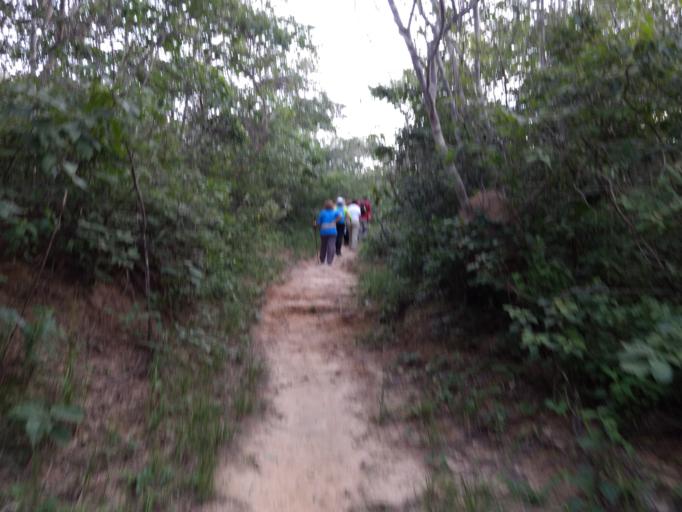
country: BR
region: Ceara
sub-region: Crateus
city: Crateus
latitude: -5.1438
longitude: -40.9221
